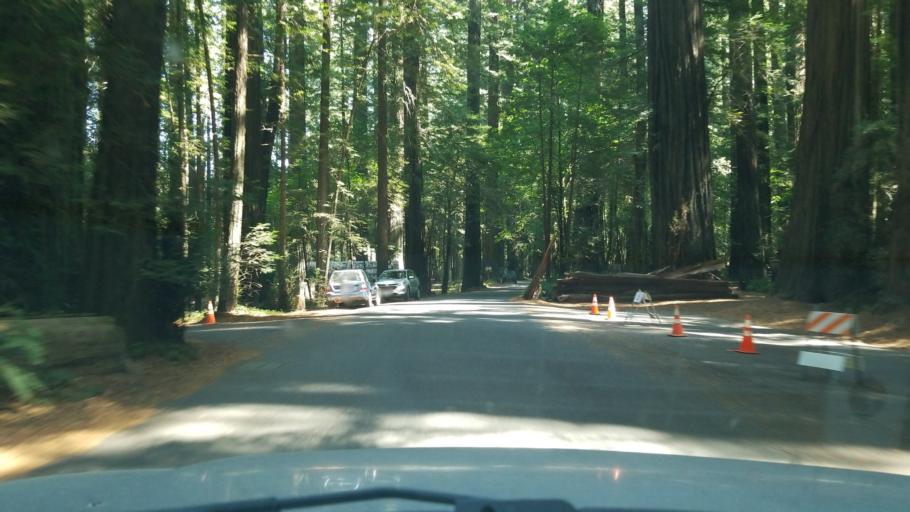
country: US
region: California
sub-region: Humboldt County
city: Rio Dell
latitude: 40.3526
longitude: -123.9249
